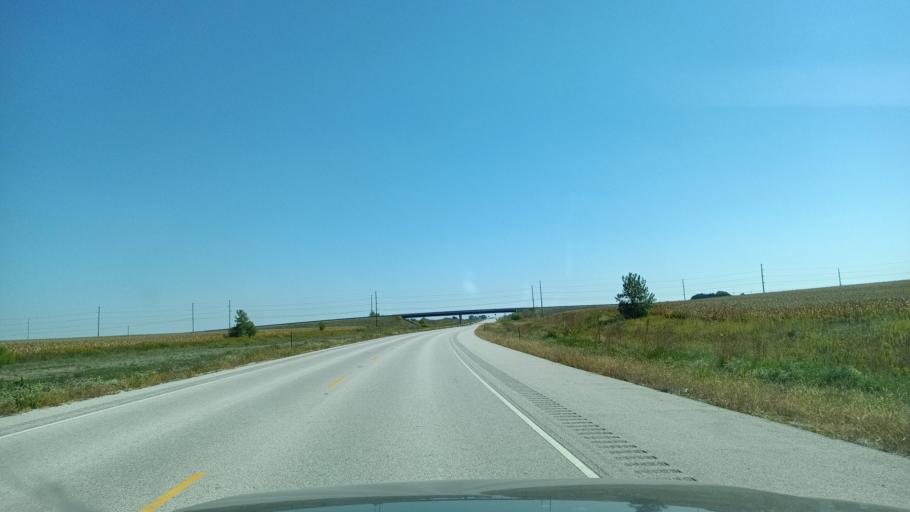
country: US
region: Illinois
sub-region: McDonough County
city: Macomb
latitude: 40.5032
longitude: -90.6992
